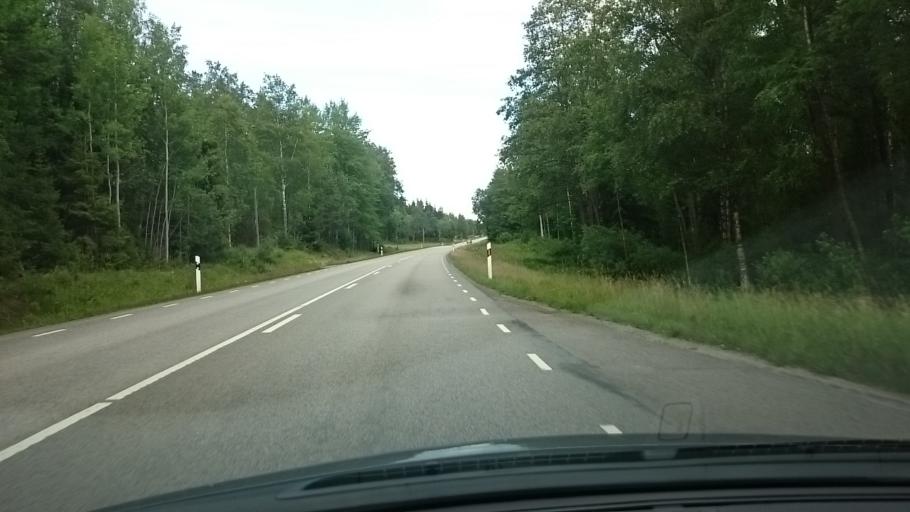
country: SE
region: Vaestra Goetaland
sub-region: Karlsborgs Kommun
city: Karlsborg
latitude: 58.6952
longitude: 14.6871
